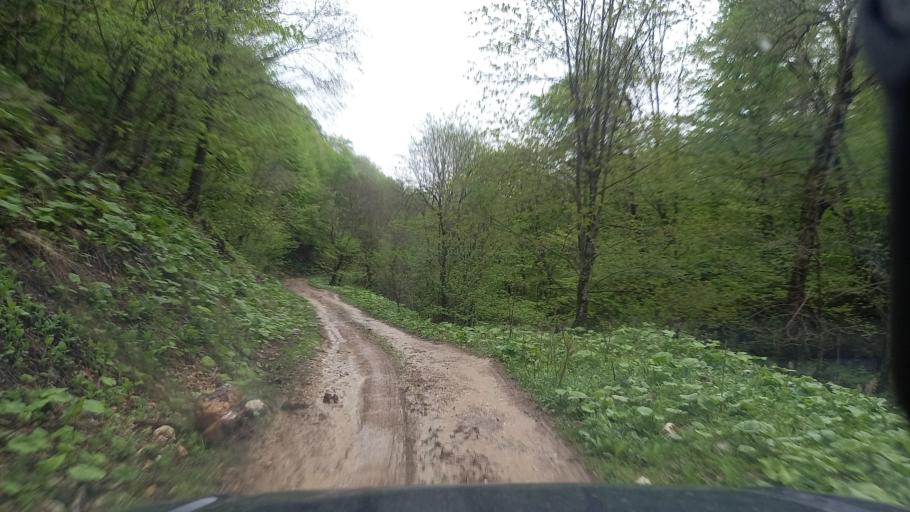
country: RU
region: Kabardino-Balkariya
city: Babugent
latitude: 43.2143
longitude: 43.5478
